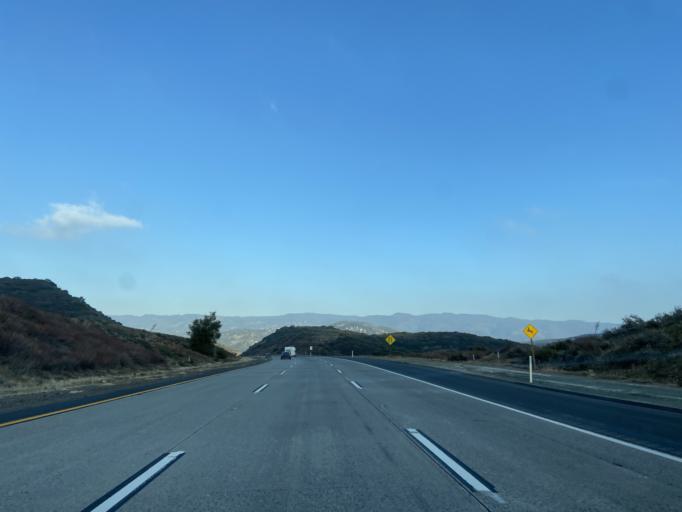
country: US
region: California
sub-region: San Diego County
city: Pine Valley
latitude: 32.8202
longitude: -116.5727
